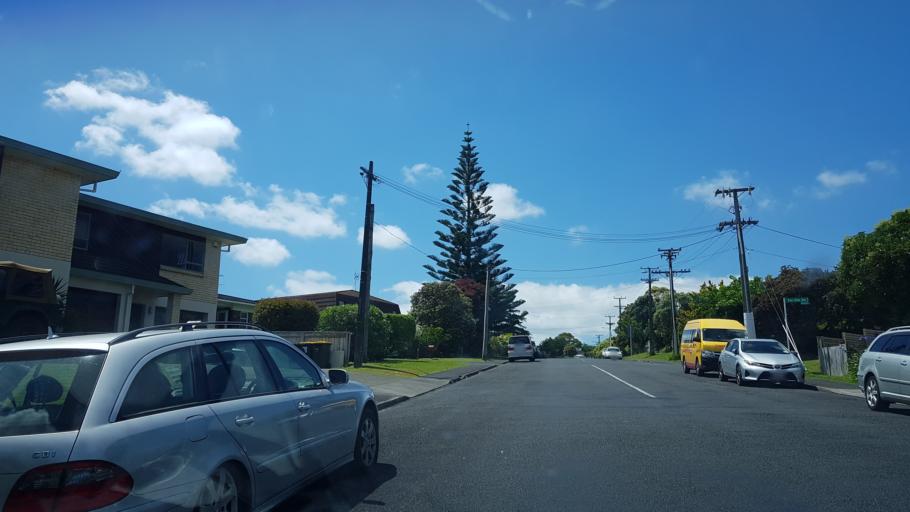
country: NZ
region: Auckland
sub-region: Auckland
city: North Shore
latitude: -36.7877
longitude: 174.7095
